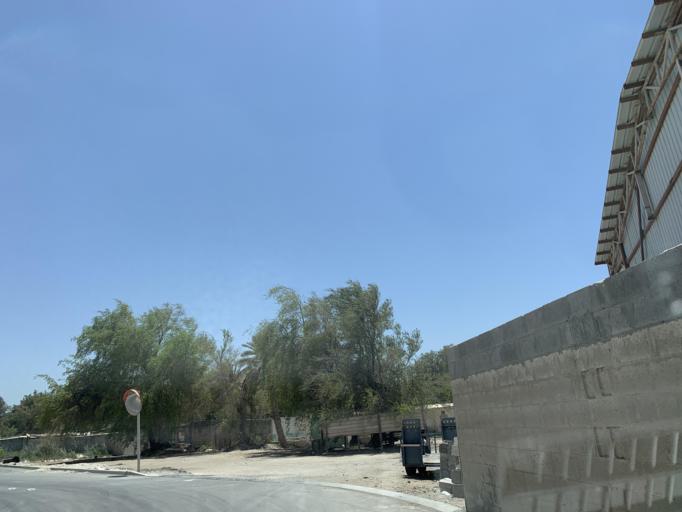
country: BH
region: Manama
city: Jidd Hafs
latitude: 26.2332
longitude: 50.4911
